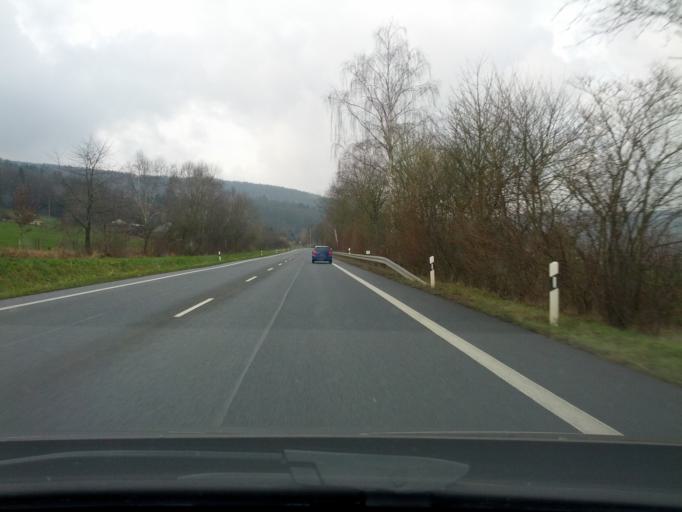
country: DE
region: Lower Saxony
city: Bodenfelde
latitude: 51.5920
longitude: 9.5702
